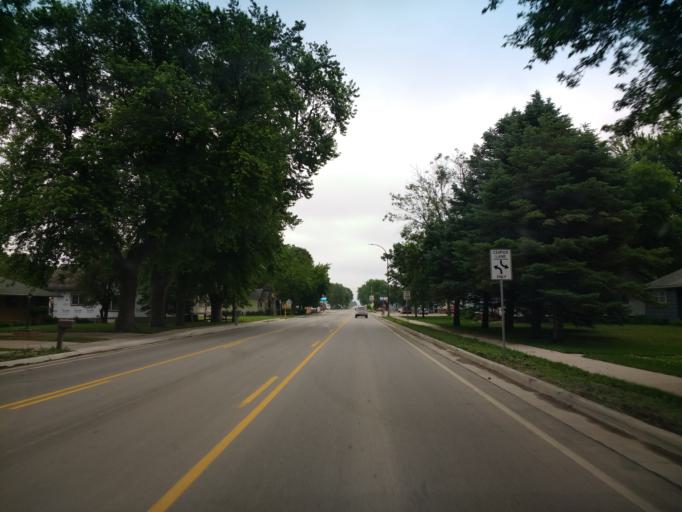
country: US
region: Iowa
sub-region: O'Brien County
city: Sanborn
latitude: 43.1860
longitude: -95.6598
